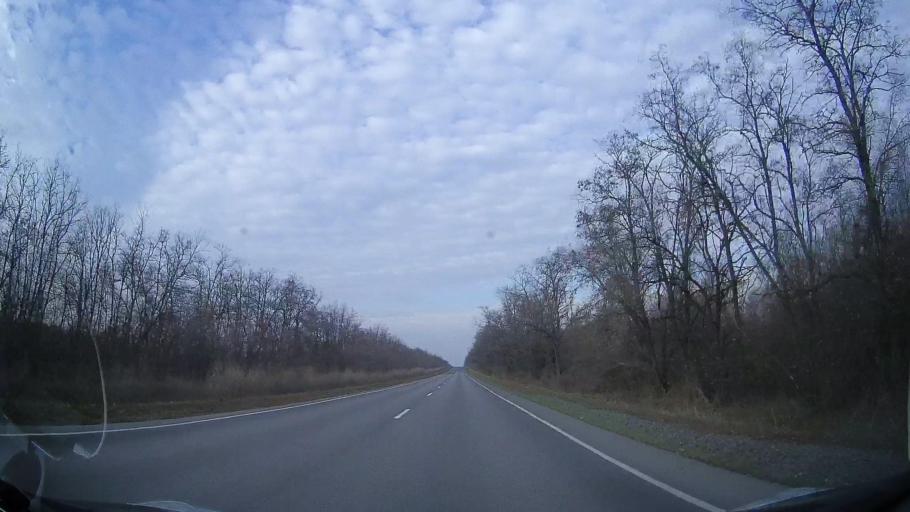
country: RU
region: Rostov
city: Bagayevskaya
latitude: 47.1187
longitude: 40.2767
